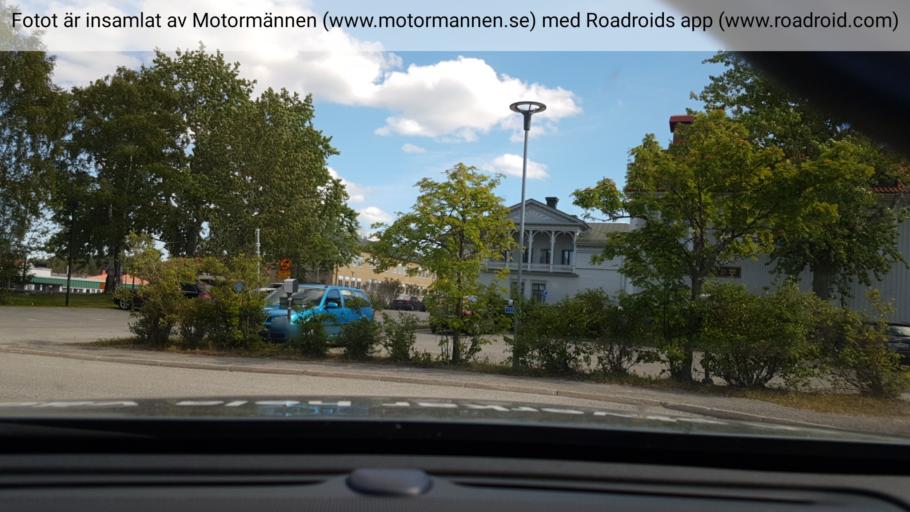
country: SE
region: Vaesterbotten
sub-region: Lycksele Kommun
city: Lycksele
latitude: 64.5953
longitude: 18.6733
